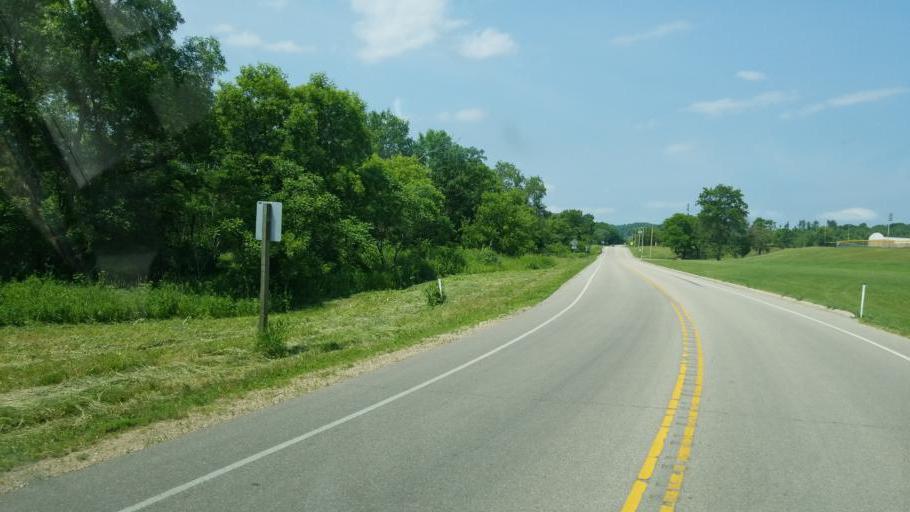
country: US
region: Wisconsin
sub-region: Vernon County
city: Viroqua
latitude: 43.4907
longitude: -90.6798
